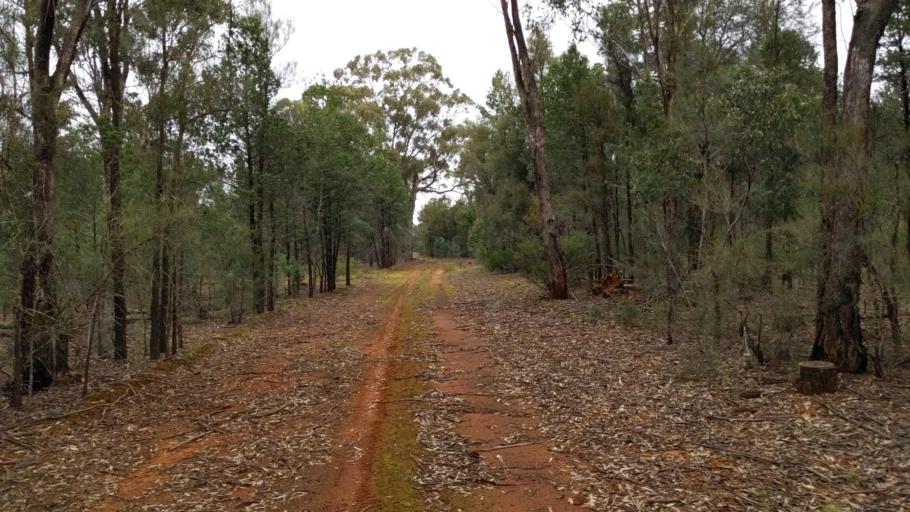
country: AU
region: New South Wales
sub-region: Coolamon
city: Coolamon
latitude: -34.8490
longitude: 146.9322
